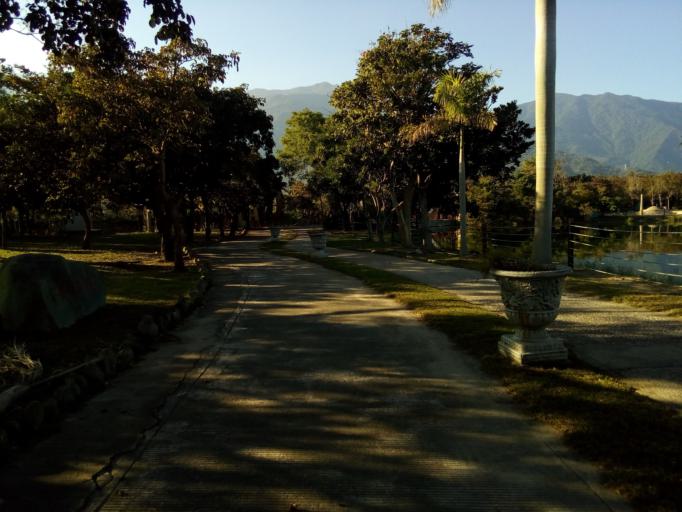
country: TW
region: Taiwan
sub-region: Taitung
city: Taitung
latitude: 23.0361
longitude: 121.1718
